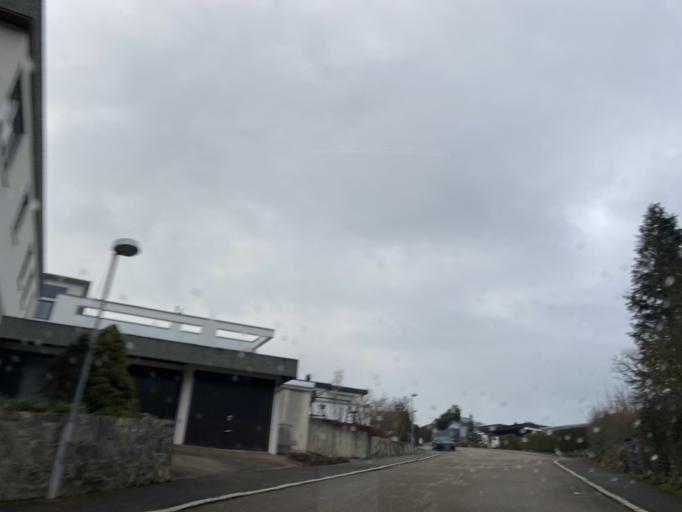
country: DE
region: Baden-Wuerttemberg
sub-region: Regierungsbezirk Stuttgart
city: Vaihingen an der Enz
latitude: 48.9152
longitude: 8.9370
